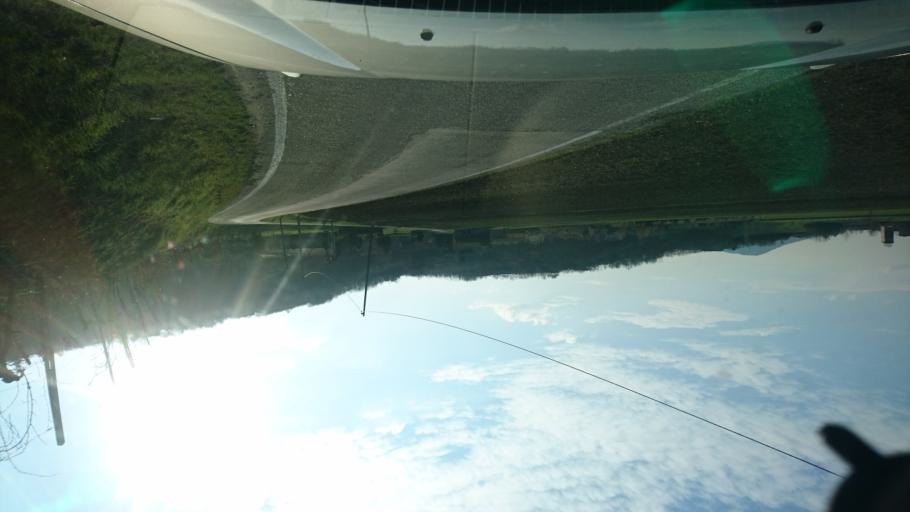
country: IT
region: Veneto
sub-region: Provincia di Padova
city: Vo
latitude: 45.3513
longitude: 11.6202
